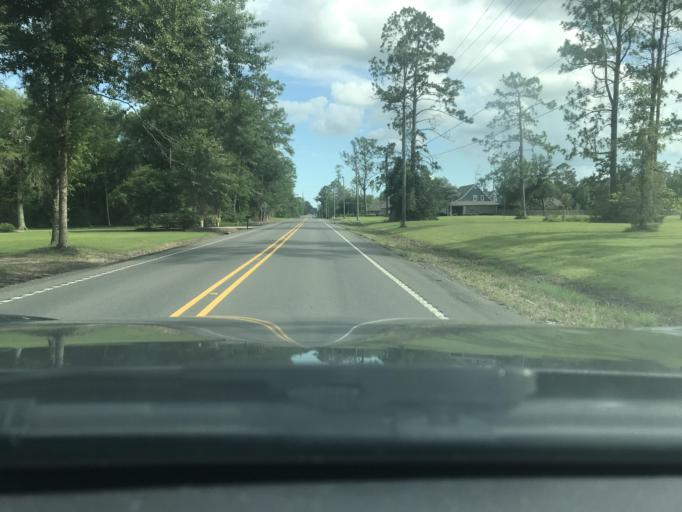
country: US
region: Louisiana
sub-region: Calcasieu Parish
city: Moss Bluff
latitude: 30.3390
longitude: -93.2581
